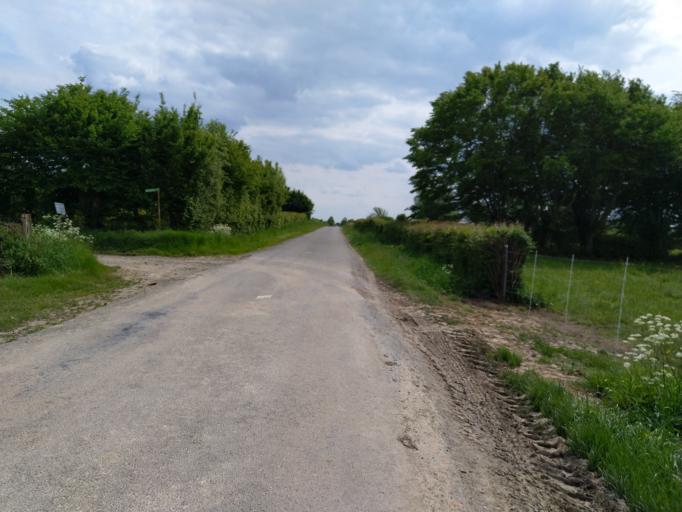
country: FR
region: Picardie
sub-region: Departement de l'Aisne
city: Boue
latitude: 50.0348
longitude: 3.6807
